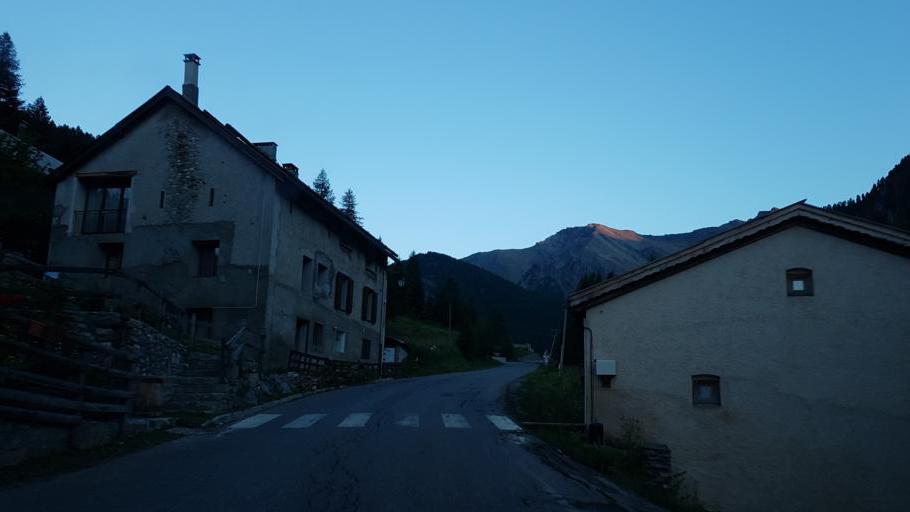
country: IT
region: Piedmont
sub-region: Provincia di Cuneo
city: Pontechianale
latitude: 44.7112
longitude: 6.8492
